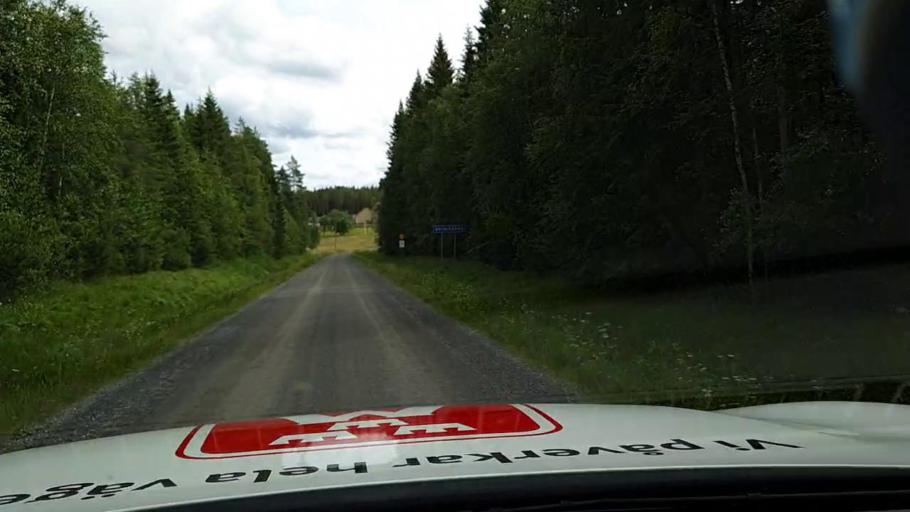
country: SE
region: Jaemtland
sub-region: Braecke Kommun
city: Braecke
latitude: 63.2854
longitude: 15.3665
